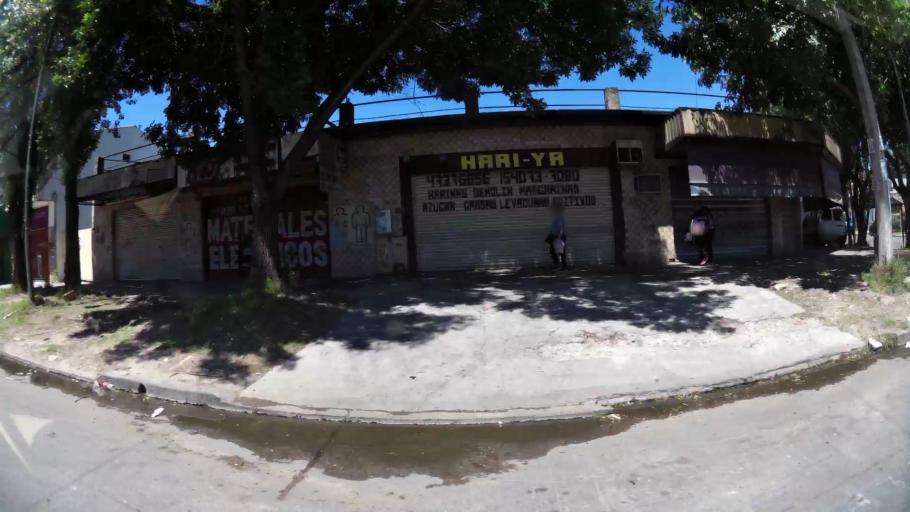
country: AR
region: Buenos Aires
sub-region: Partido de Tigre
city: Tigre
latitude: -34.5032
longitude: -58.5849
